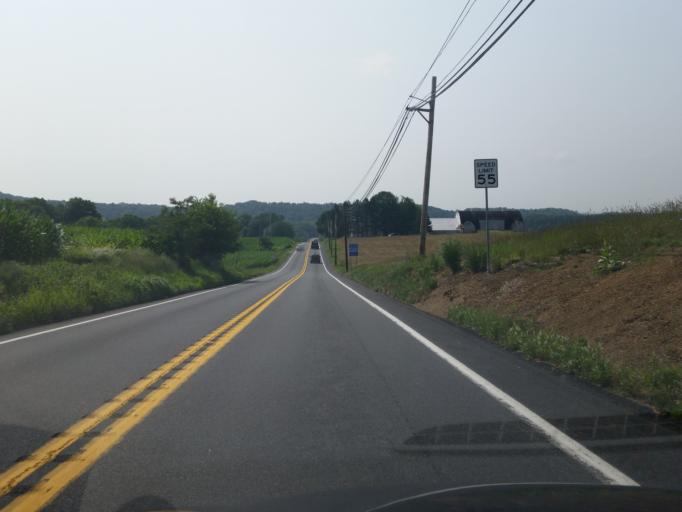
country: US
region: Pennsylvania
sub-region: Dauphin County
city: Palmdale
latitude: 40.3296
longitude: -76.6366
